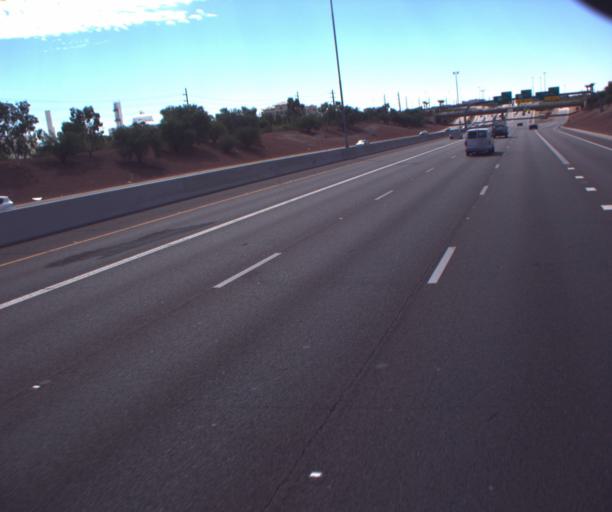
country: US
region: Arizona
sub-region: Maricopa County
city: Chandler
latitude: 33.3030
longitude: -111.8944
